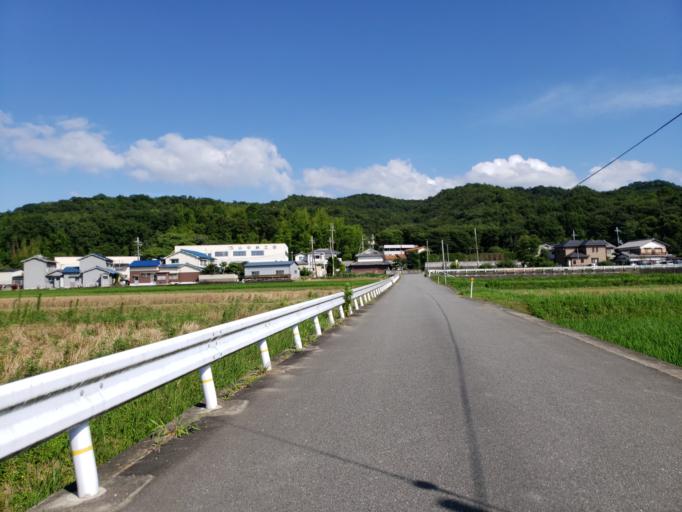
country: JP
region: Hyogo
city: Himeji
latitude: 34.9070
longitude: 134.7701
